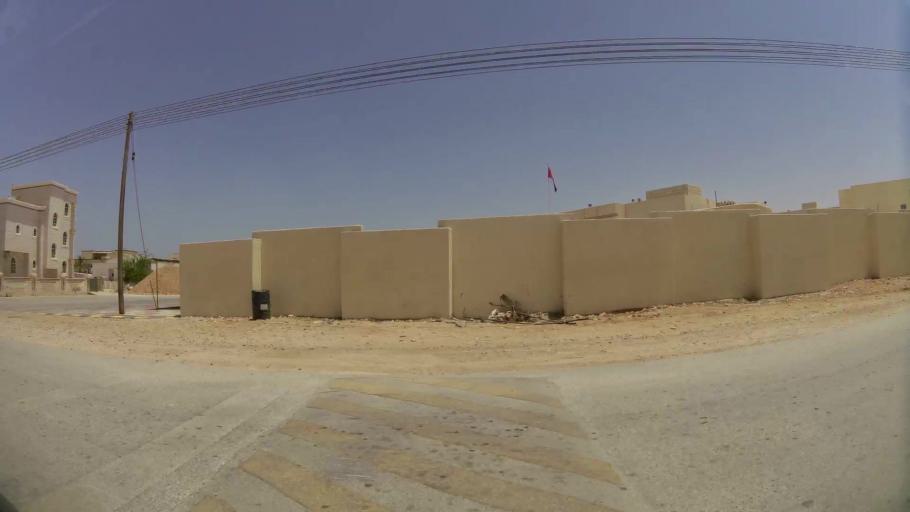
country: OM
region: Zufar
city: Salalah
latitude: 17.0725
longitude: 54.1501
